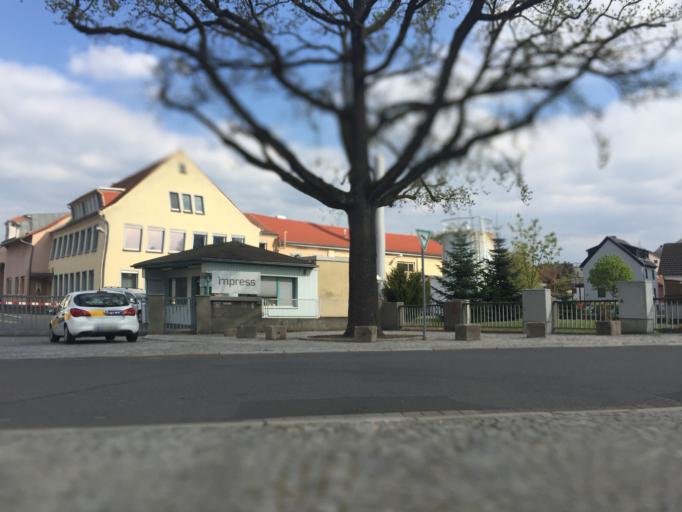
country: DE
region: Bavaria
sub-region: Regierungsbezirk Unterfranken
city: Glattbach
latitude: 49.9878
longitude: 9.1363
